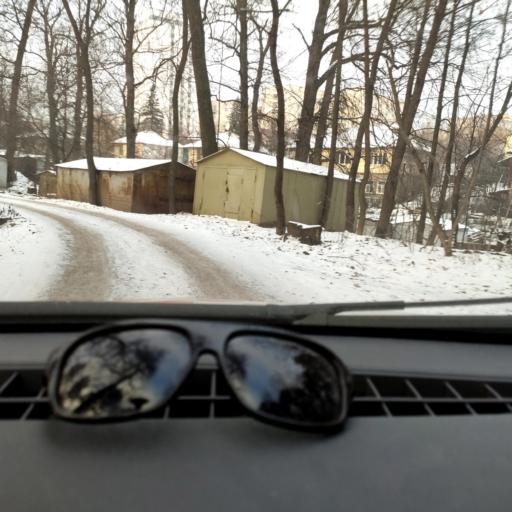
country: RU
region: Bashkortostan
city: Ufa
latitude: 54.7471
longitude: 56.0058
